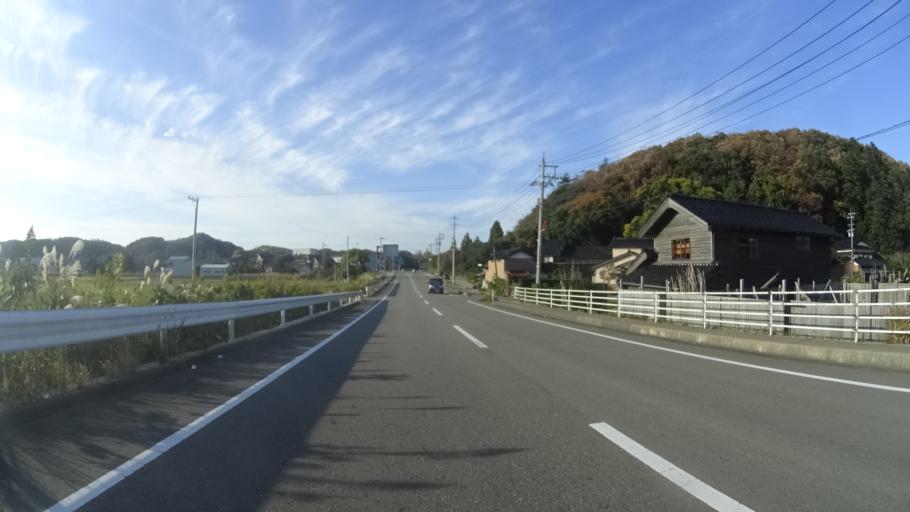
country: JP
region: Ishikawa
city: Hakui
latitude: 37.0208
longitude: 136.7888
